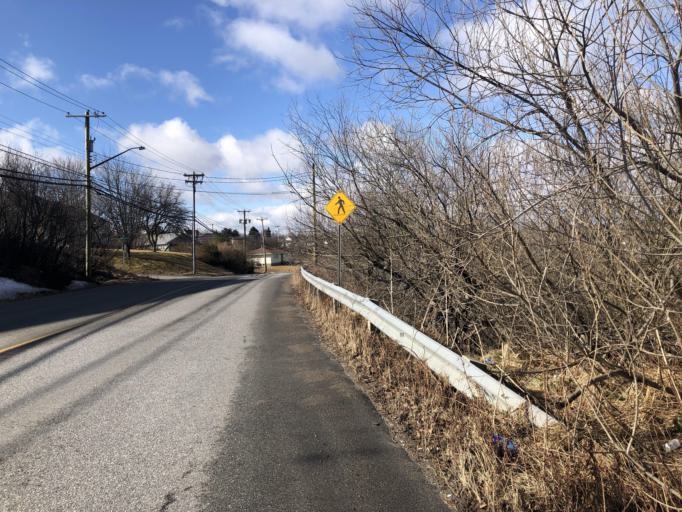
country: CA
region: New Brunswick
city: Saint John
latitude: 45.3206
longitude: -66.0029
